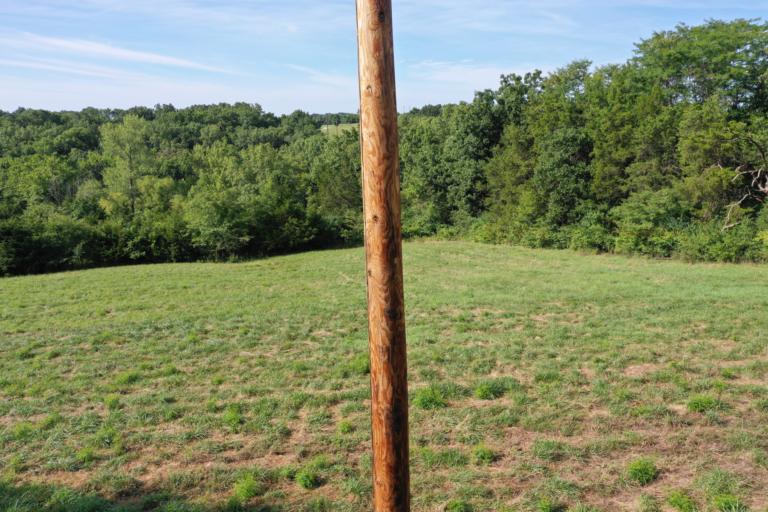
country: US
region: Missouri
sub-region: Callaway County
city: Holts Summit
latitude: 38.5354
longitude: -92.0518
